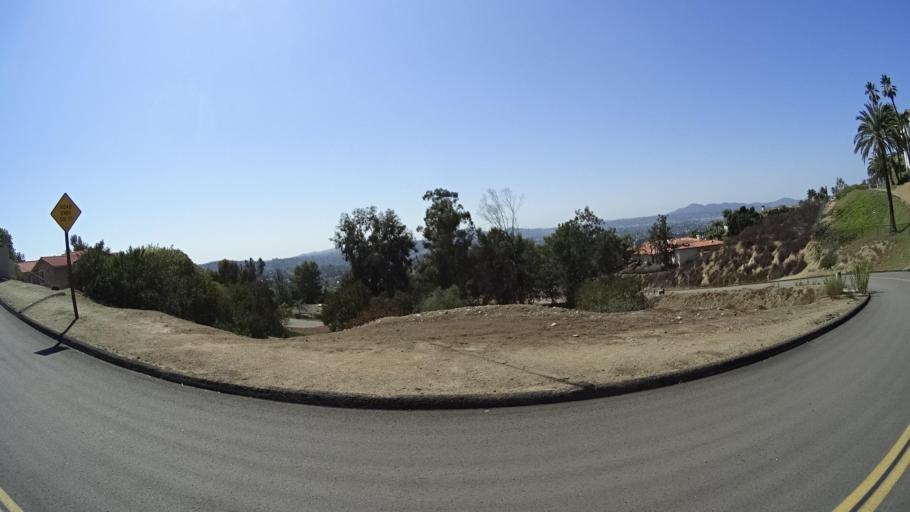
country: US
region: California
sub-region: San Diego County
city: Granite Hills
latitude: 32.8034
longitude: -116.8929
